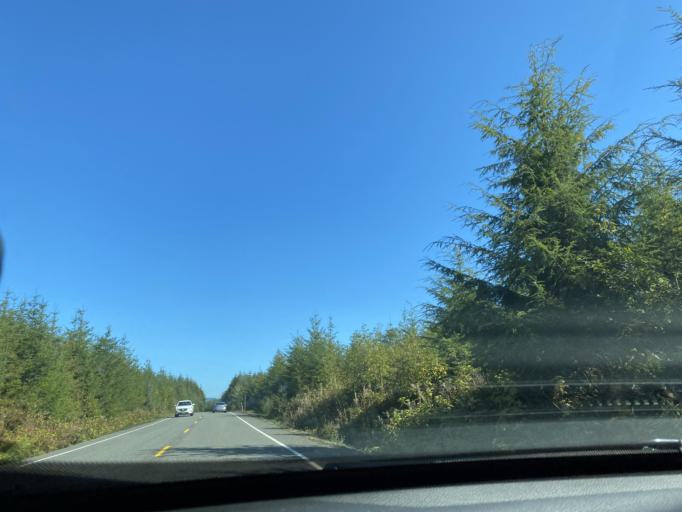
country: US
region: Washington
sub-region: Clallam County
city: Forks
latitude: 47.9260
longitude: -124.4928
